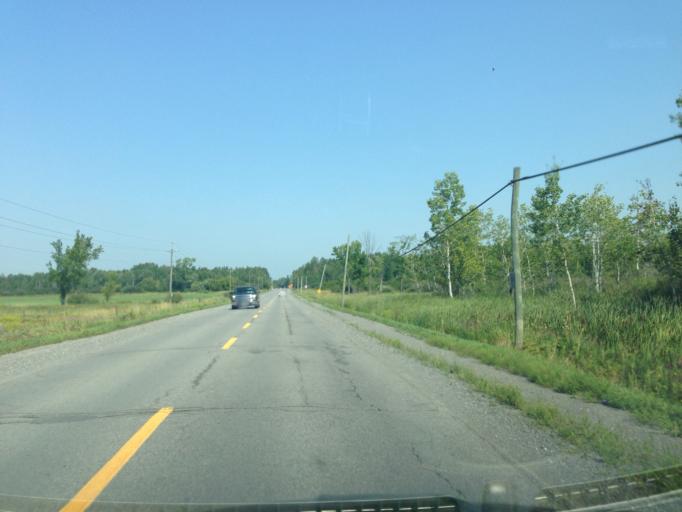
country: CA
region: Ontario
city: Ottawa
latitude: 45.4132
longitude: -75.5637
